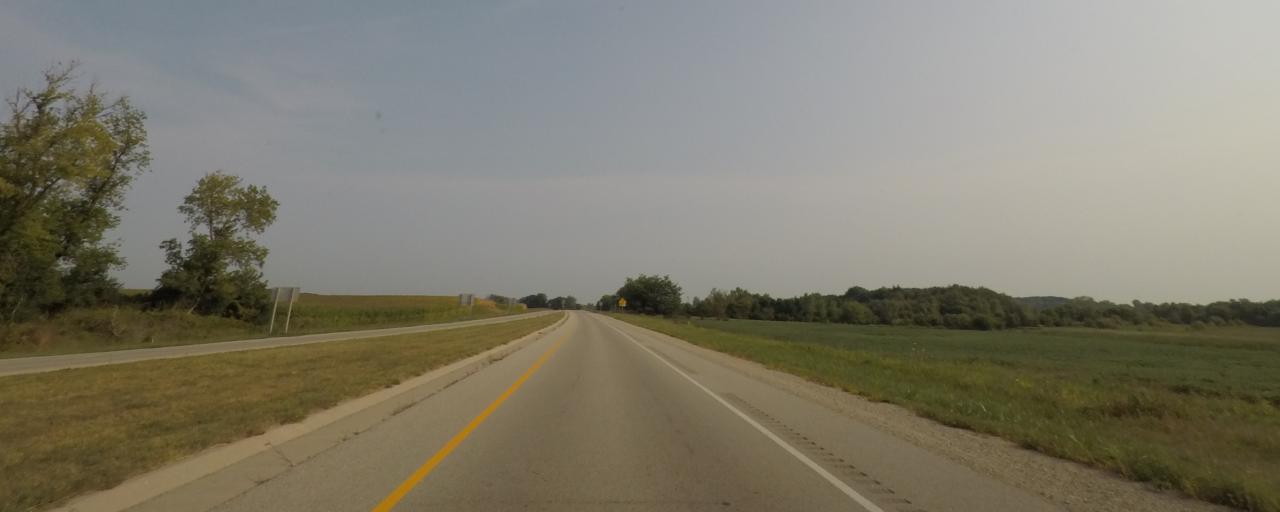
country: US
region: Wisconsin
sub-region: Dane County
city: Deerfield
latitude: 43.0316
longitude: -89.0770
